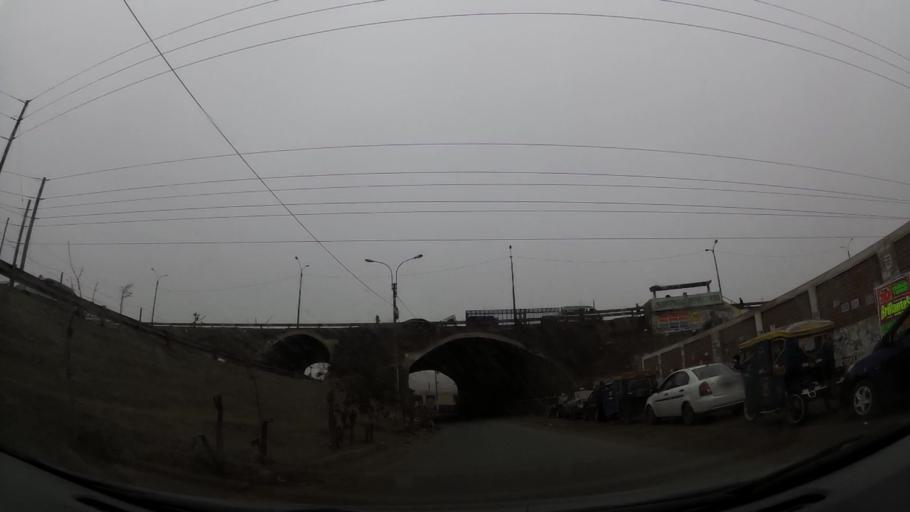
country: PE
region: Lima
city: Ventanilla
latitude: -11.8368
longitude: -77.1102
